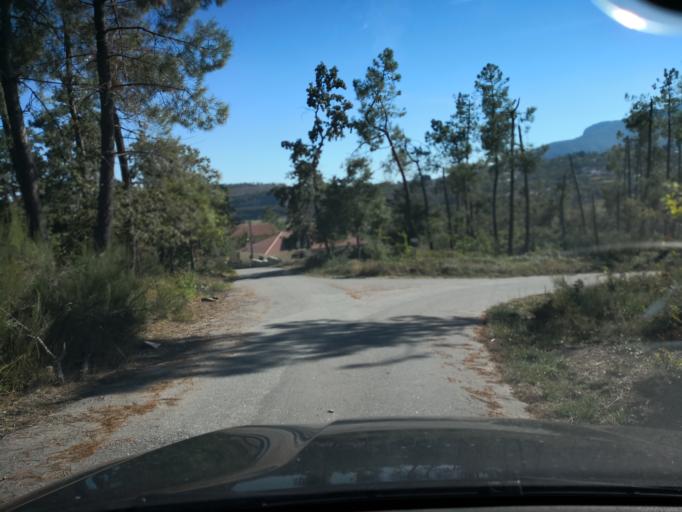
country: PT
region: Vila Real
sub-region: Santa Marta de Penaguiao
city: Santa Marta de Penaguiao
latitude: 41.2931
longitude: -7.8621
